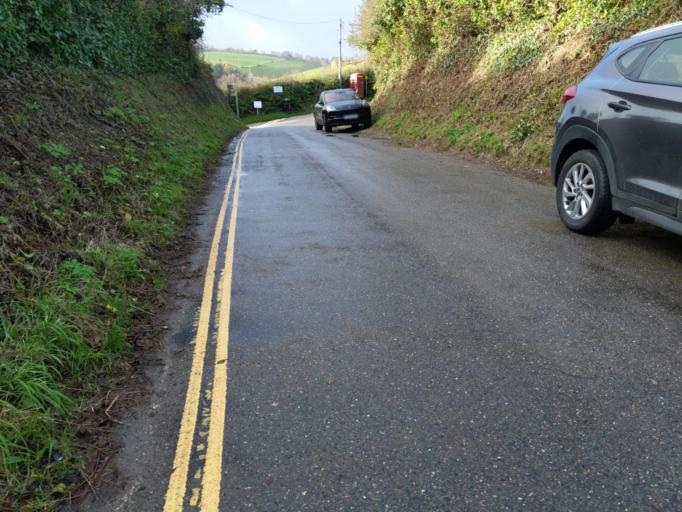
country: GB
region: England
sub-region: Cornwall
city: Looe
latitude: 50.3375
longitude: -4.4964
